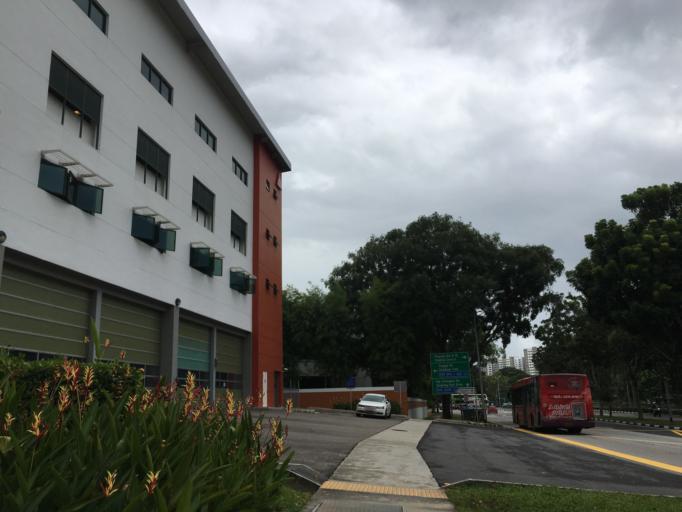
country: MY
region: Johor
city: Kampung Pasir Gudang Baru
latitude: 1.3801
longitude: 103.8953
